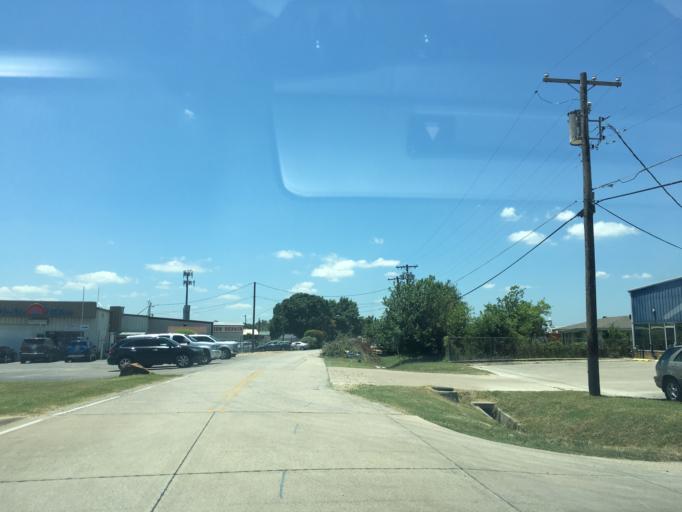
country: US
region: Texas
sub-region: Dallas County
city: Garland
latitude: 32.8463
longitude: -96.6837
